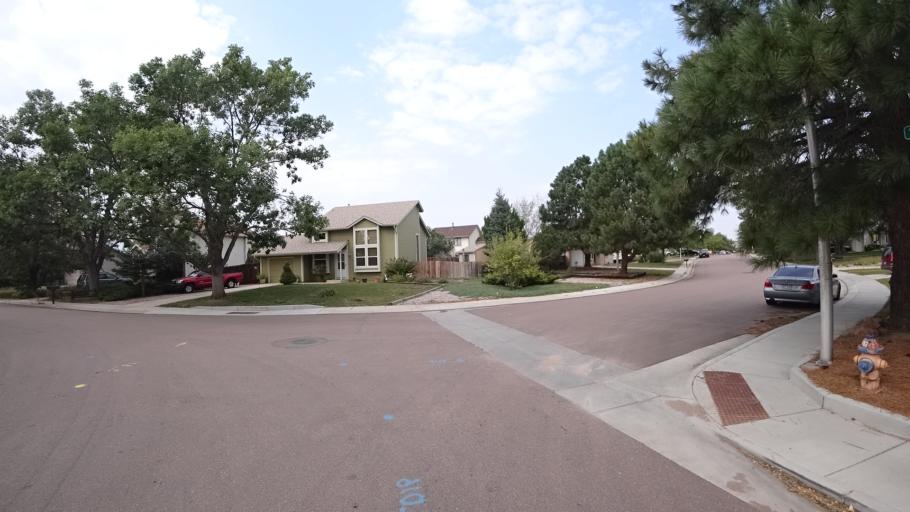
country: US
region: Colorado
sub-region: El Paso County
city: Stratmoor
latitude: 38.8179
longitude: -104.7441
